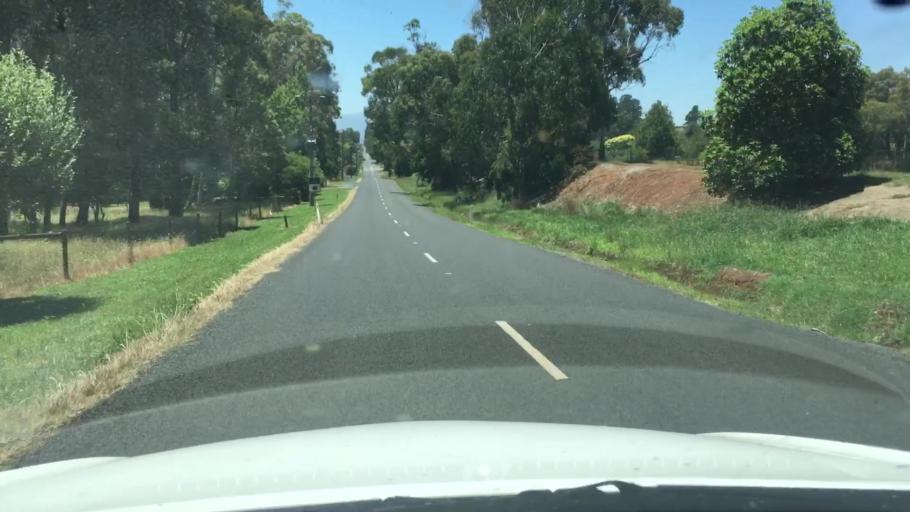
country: AU
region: Victoria
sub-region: Yarra Ranges
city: Mount Evelyn
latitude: -37.8049
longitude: 145.4385
